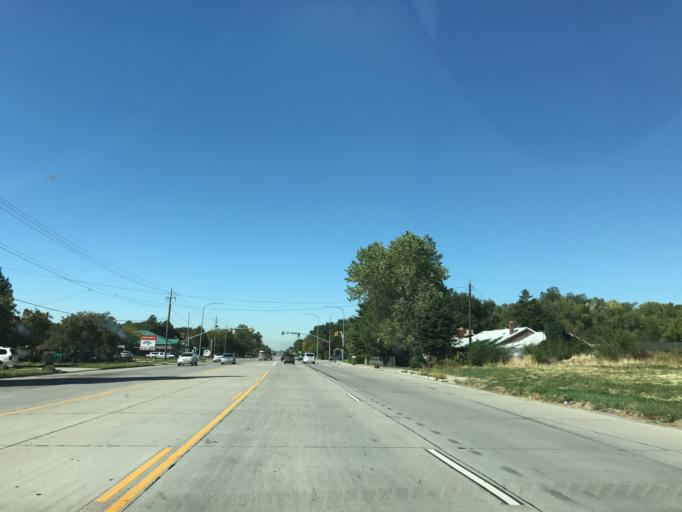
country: US
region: Utah
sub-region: Weber County
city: Ogden
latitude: 41.2441
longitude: -111.9515
